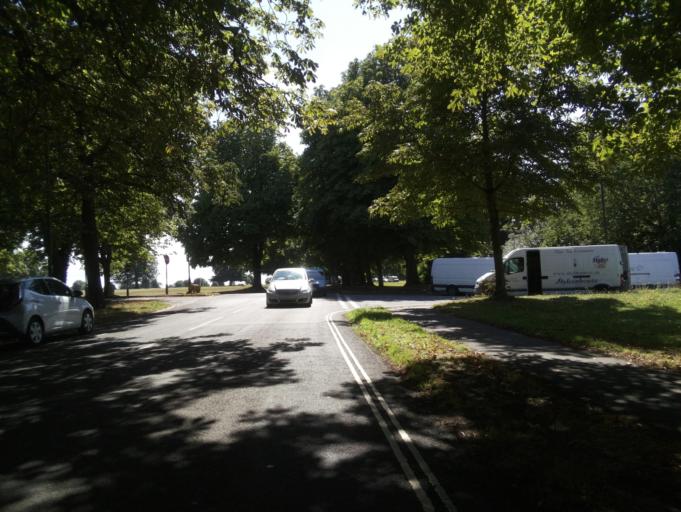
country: GB
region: England
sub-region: Bristol
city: Bristol
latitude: 51.4788
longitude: -2.6191
